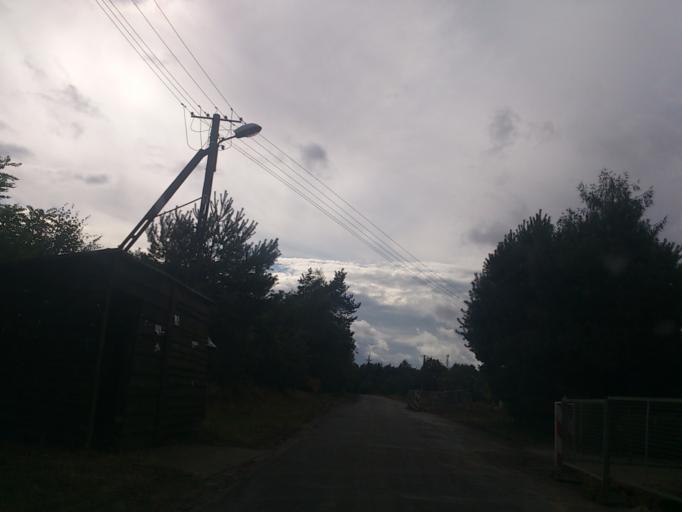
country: PL
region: Greater Poland Voivodeship
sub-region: Powiat poznanski
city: Kobylnica
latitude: 52.5190
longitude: 17.1443
